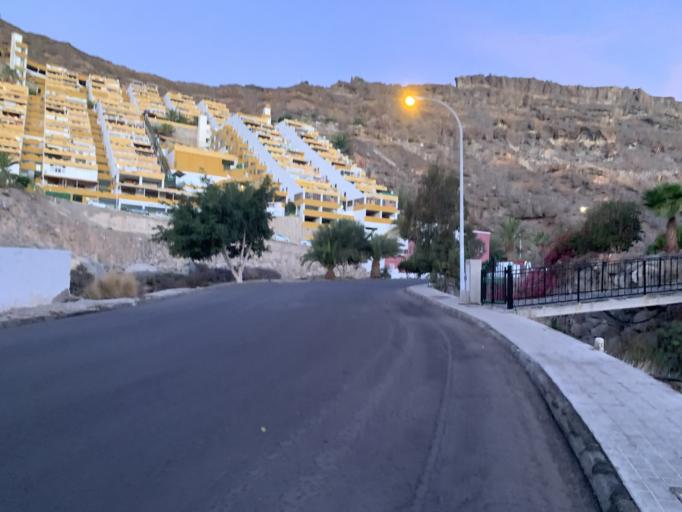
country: ES
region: Canary Islands
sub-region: Provincia de Las Palmas
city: Puerto Rico
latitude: 27.8029
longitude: -15.7319
